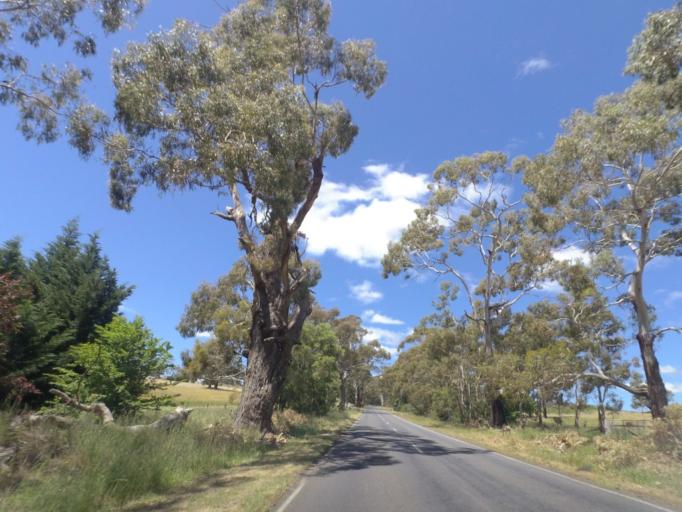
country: AU
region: Victoria
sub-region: Mount Alexander
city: Castlemaine
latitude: -37.2910
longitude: 144.2595
